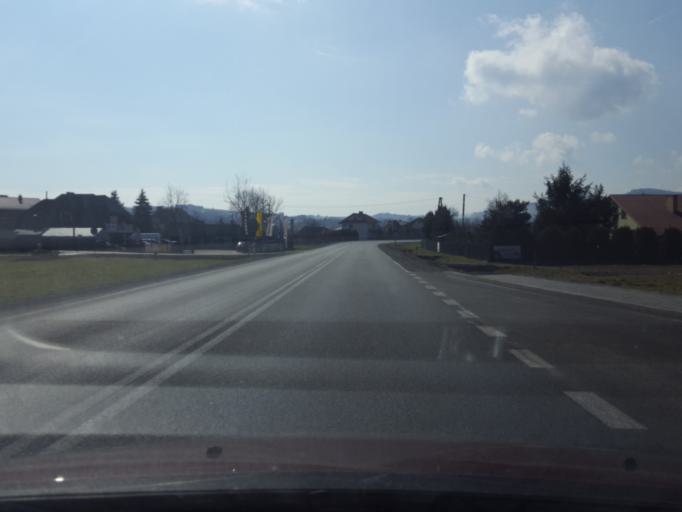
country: PL
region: Lesser Poland Voivodeship
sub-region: Powiat nowosadecki
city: Lososina Dolna
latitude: 49.7579
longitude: 20.6355
